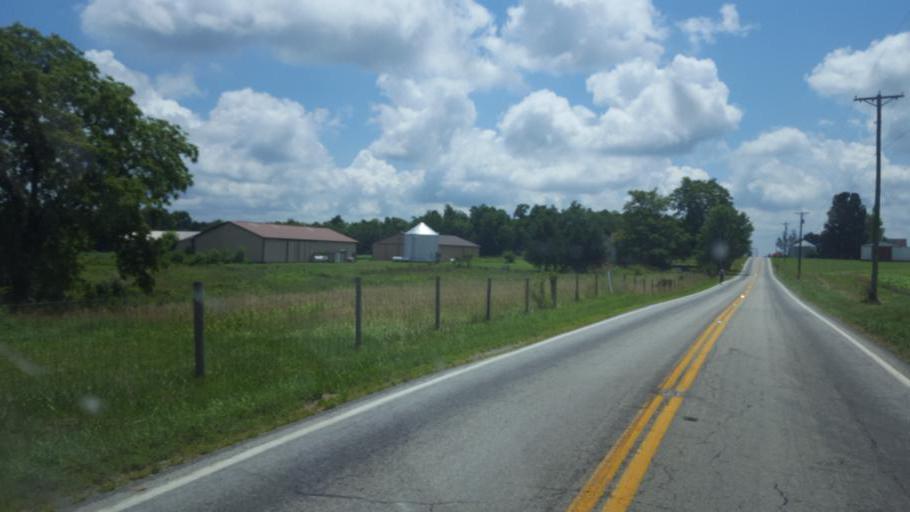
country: US
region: Ohio
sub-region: Highland County
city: Greenfield
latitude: 39.2381
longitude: -83.4306
